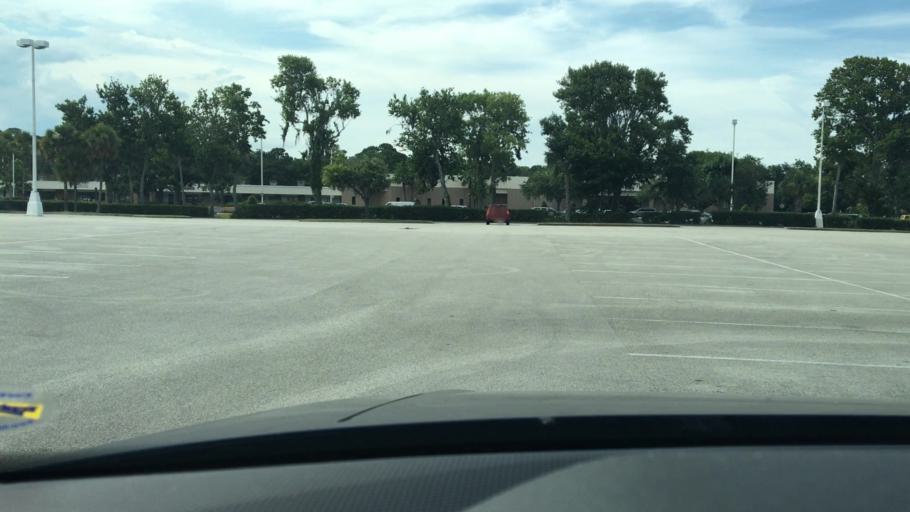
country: US
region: Florida
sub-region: Volusia County
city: Daytona Beach
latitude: 29.1983
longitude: -81.0650
